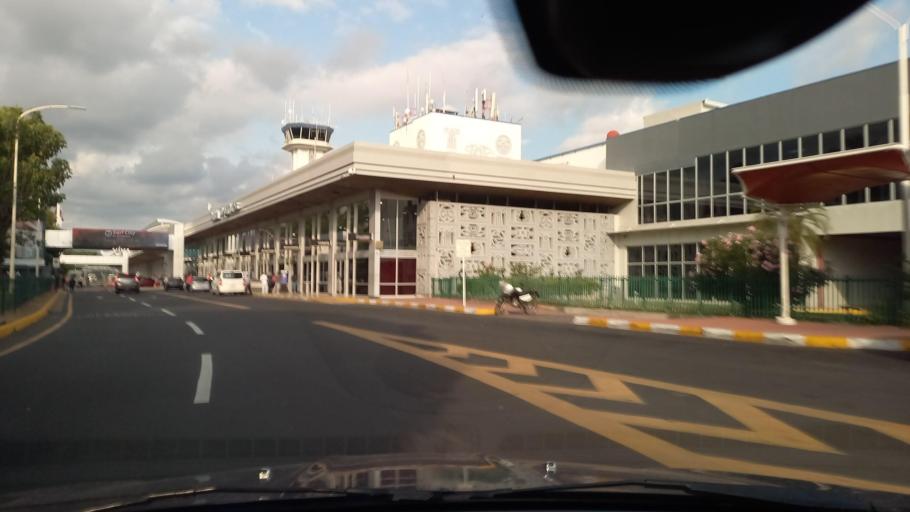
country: SV
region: La Paz
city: El Rosario
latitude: 13.4447
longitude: -89.0585
